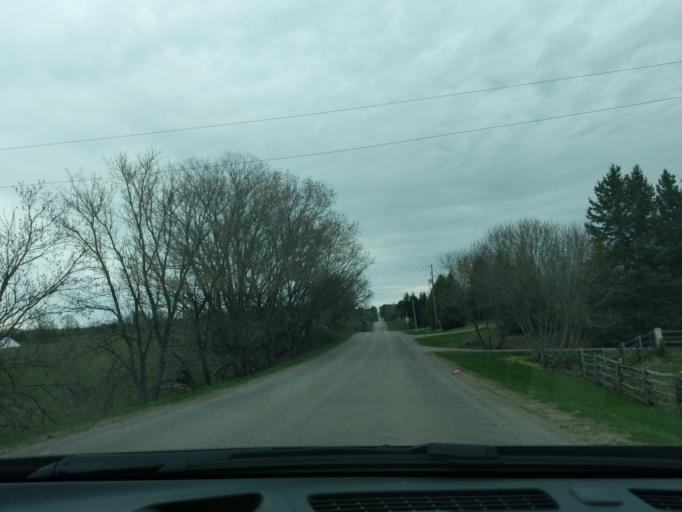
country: CA
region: Ontario
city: Orangeville
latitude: 44.0103
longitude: -79.9662
